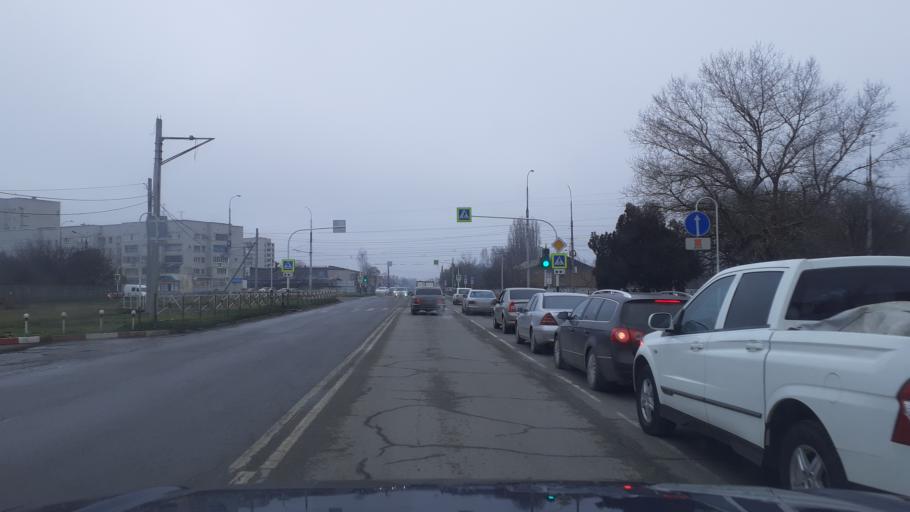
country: RU
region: Adygeya
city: Maykop
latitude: 44.6217
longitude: 40.0689
